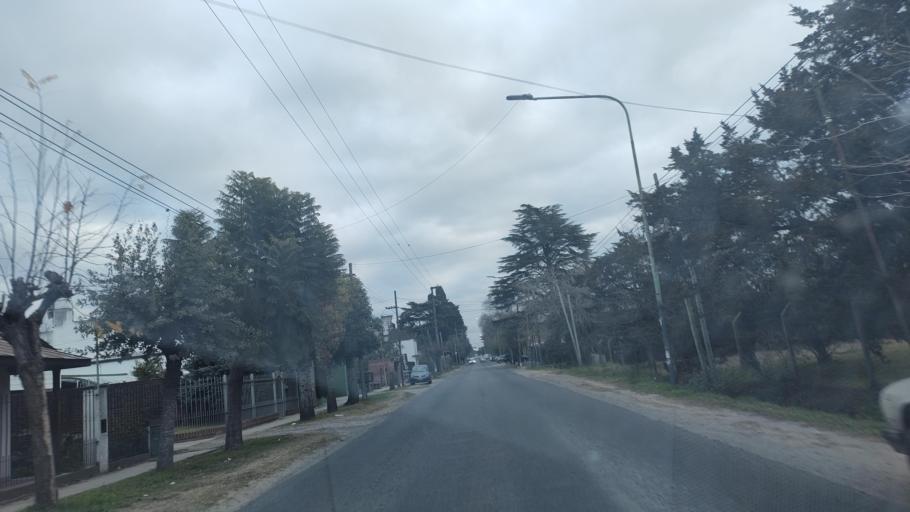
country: AR
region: Buenos Aires
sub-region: Partido de La Plata
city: La Plata
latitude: -34.8667
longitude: -58.0944
